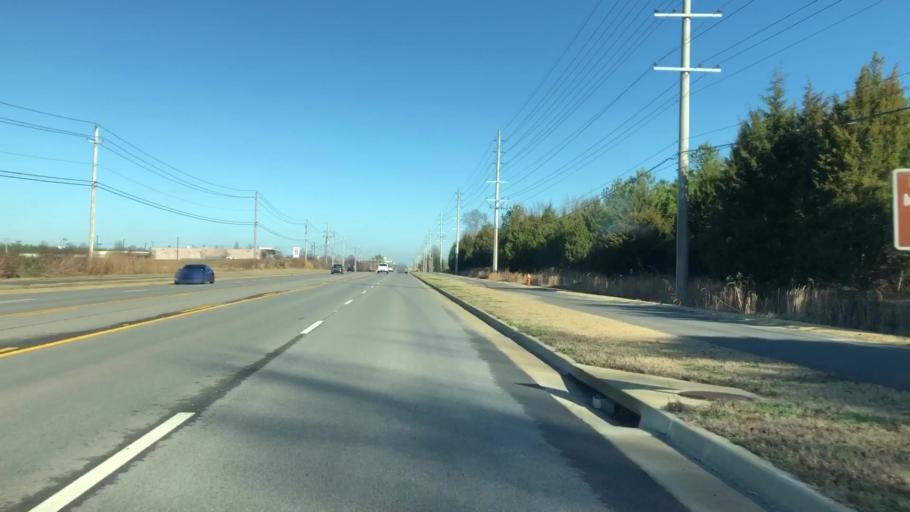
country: US
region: Alabama
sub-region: Madison County
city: Madison
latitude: 34.7256
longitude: -86.7863
